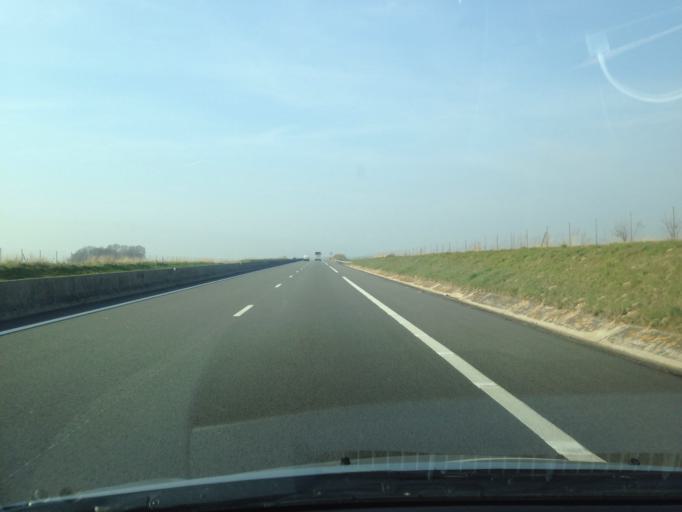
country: FR
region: Picardie
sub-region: Departement de la Somme
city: Rue
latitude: 50.3102
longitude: 1.7235
